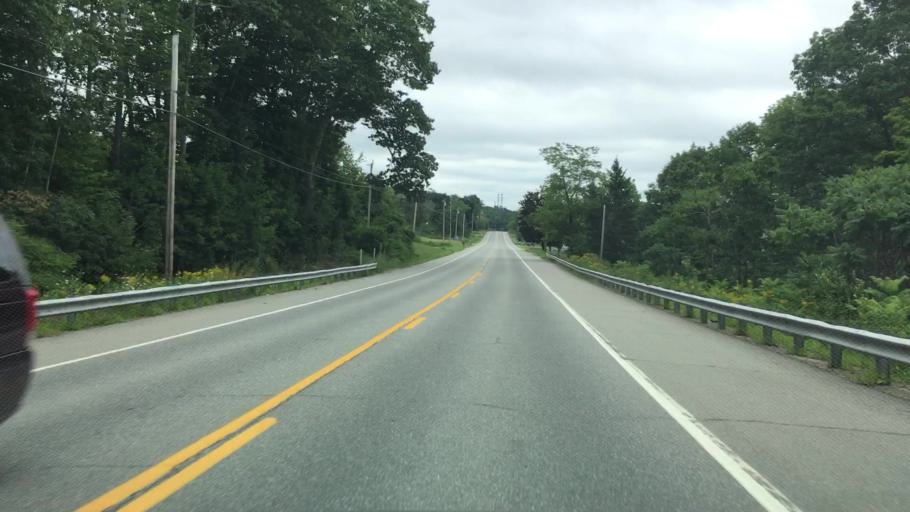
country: US
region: Maine
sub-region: Waldo County
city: Winterport
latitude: 44.6547
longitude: -68.8372
